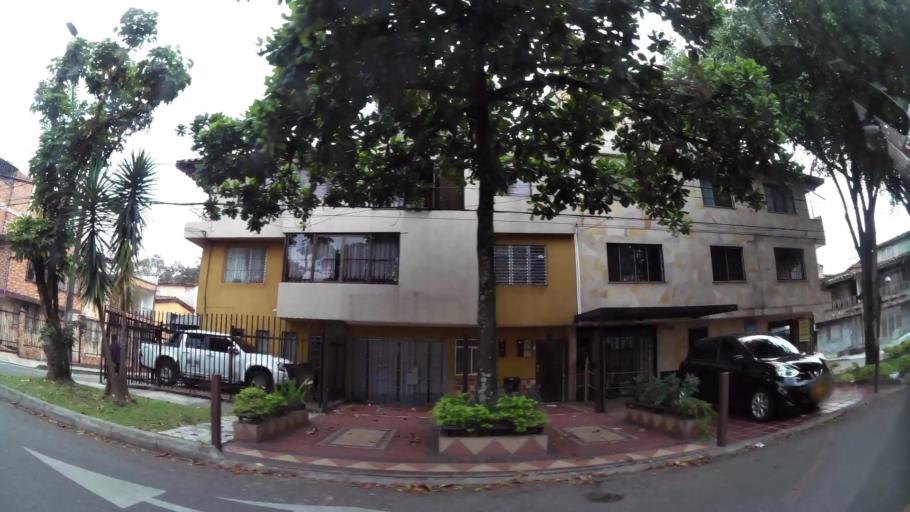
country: CO
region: Antioquia
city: Itagui
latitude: 6.2096
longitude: -75.5864
